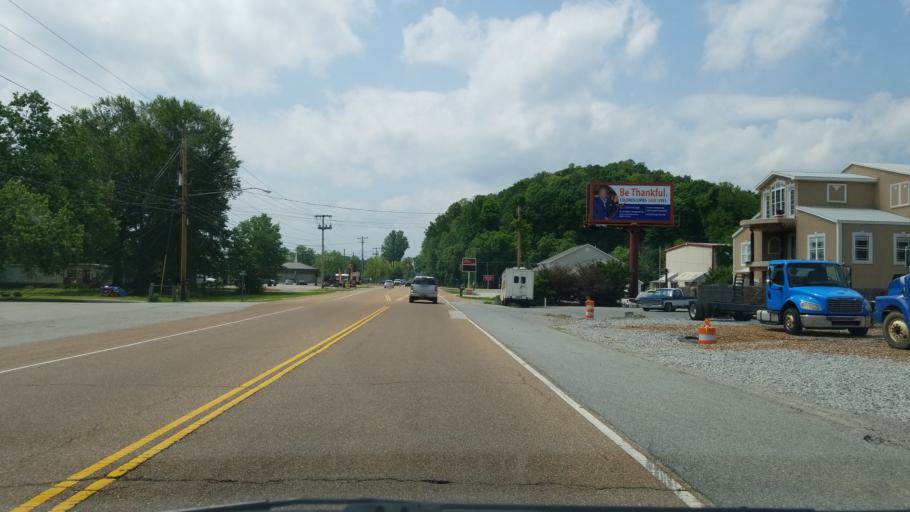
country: US
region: Tennessee
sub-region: Hamilton County
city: Falling Water
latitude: 35.2175
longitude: -85.2267
